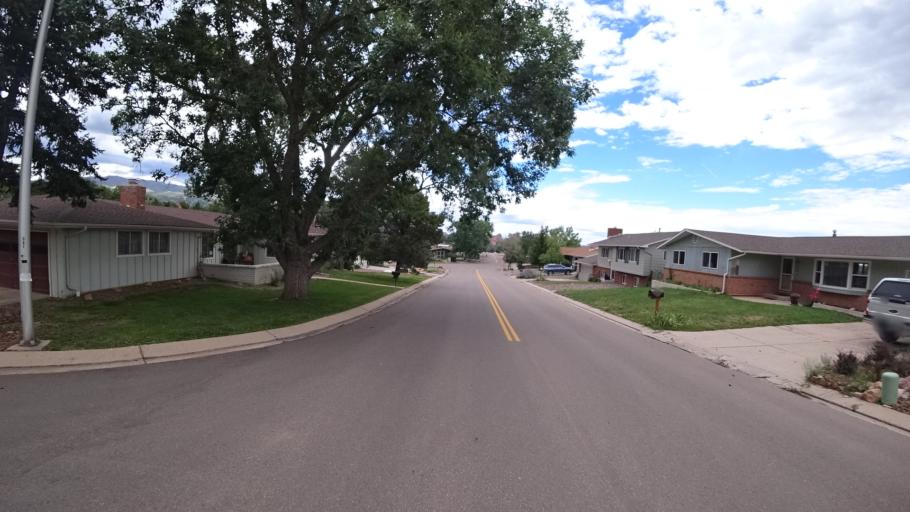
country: US
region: Colorado
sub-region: El Paso County
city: Manitou Springs
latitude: 38.8492
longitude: -104.8910
